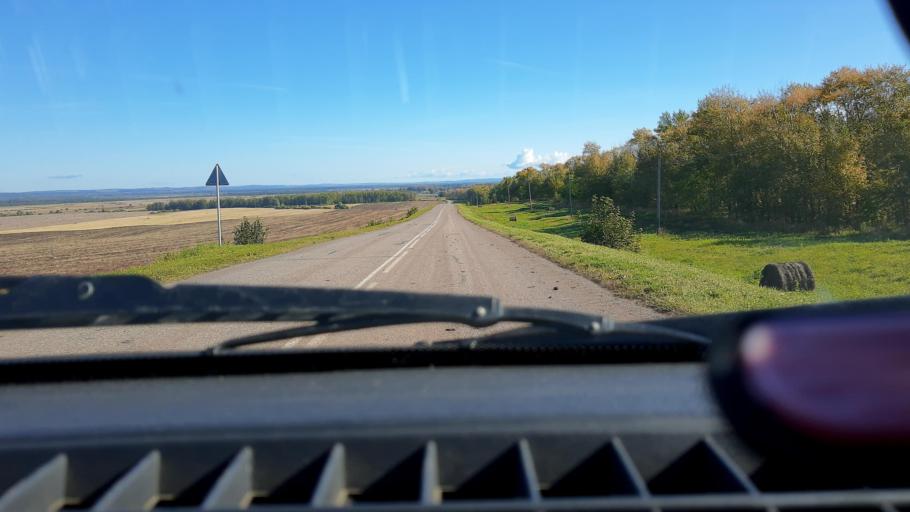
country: RU
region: Bashkortostan
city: Kushnarenkovo
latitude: 55.0747
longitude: 55.4592
